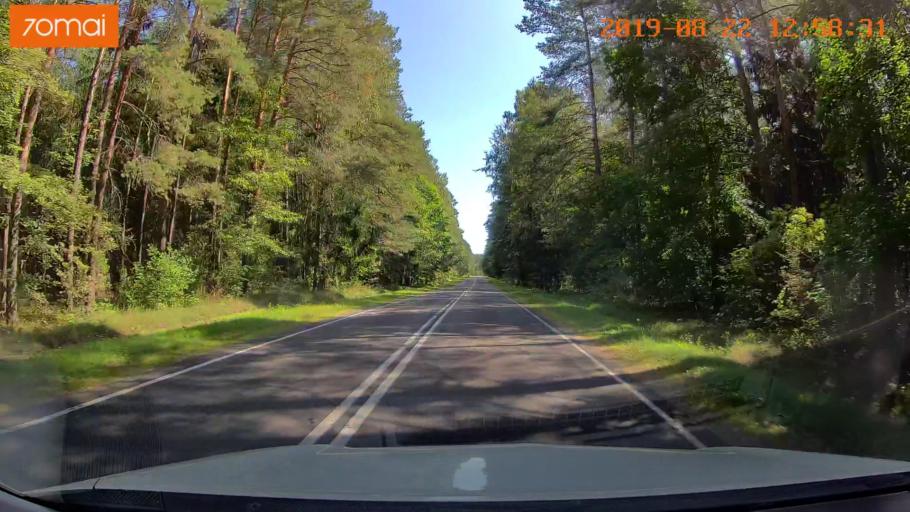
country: BY
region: Minsk
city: Prawdzinski
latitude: 53.4236
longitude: 27.7724
